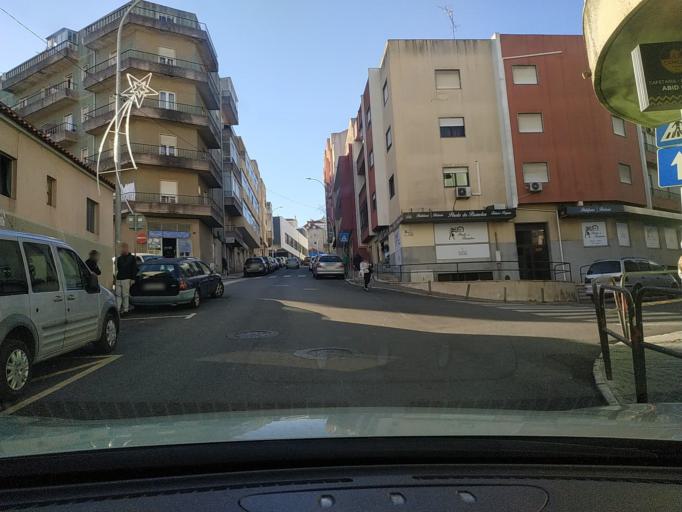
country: PT
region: Lisbon
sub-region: Odivelas
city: Pontinha
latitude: 38.7680
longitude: -9.2142
